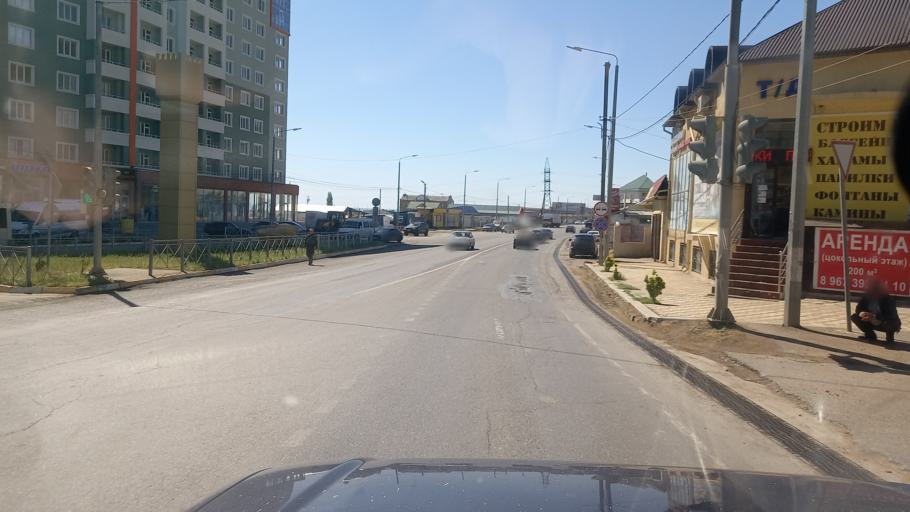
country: RU
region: Dagestan
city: Derbent
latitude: 42.0356
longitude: 48.2940
